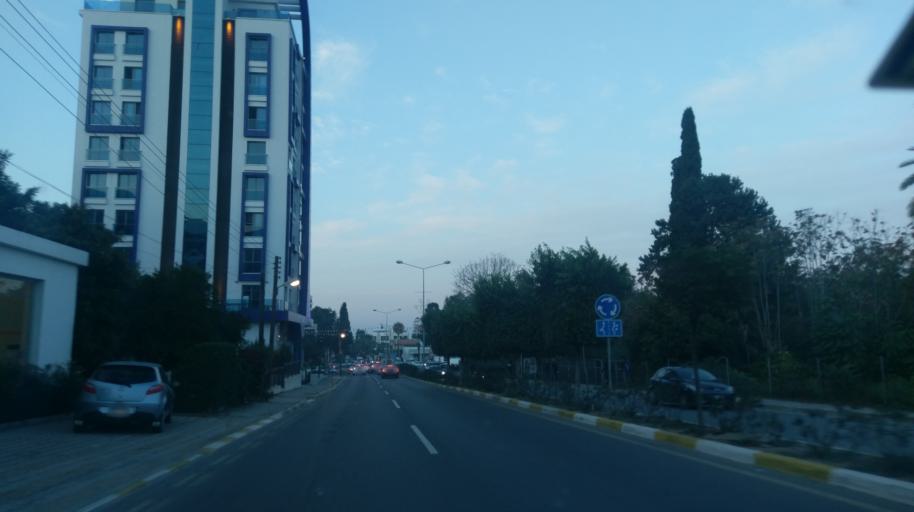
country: CY
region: Keryneia
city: Kyrenia
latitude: 35.3311
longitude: 33.3193
